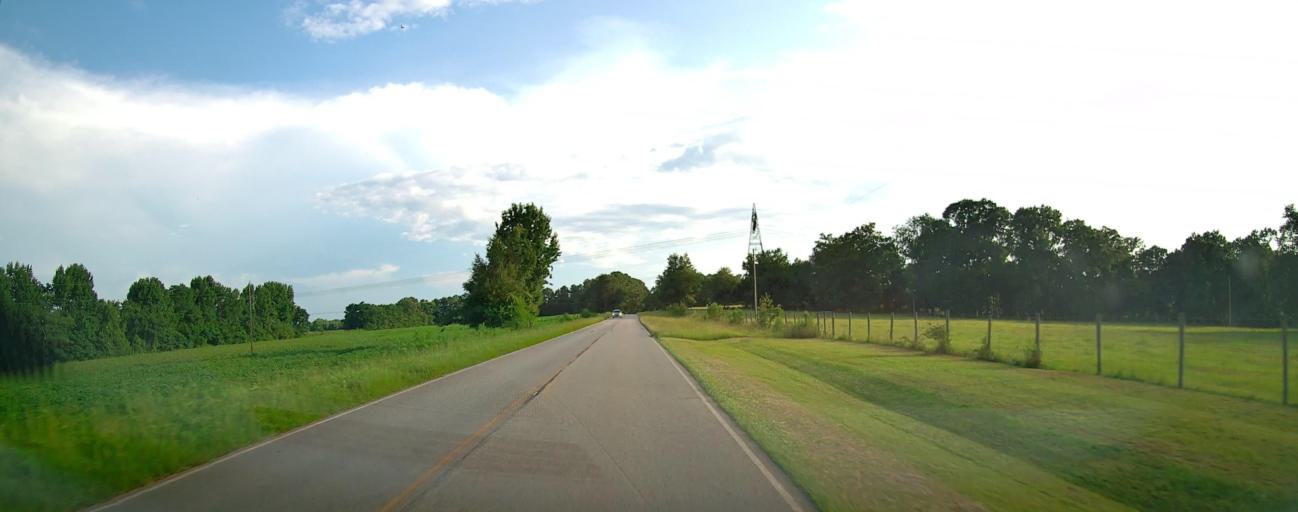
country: US
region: Georgia
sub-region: Peach County
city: Byron
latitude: 32.6923
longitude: -83.8526
